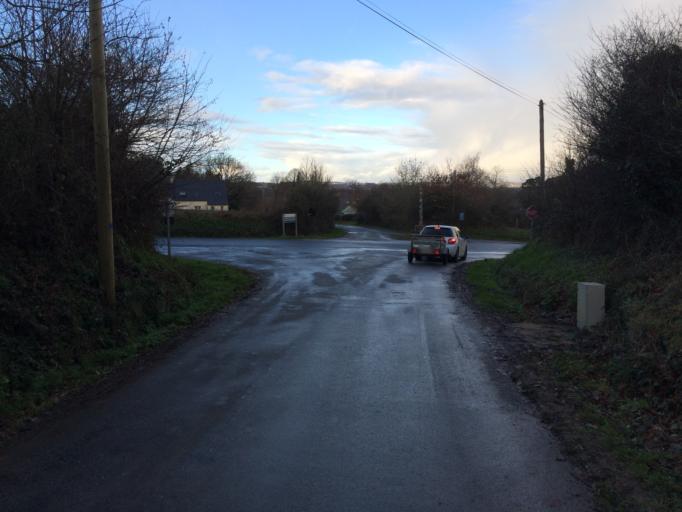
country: FR
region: Brittany
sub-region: Departement du Finistere
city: Daoulas
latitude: 48.3369
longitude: -4.2686
